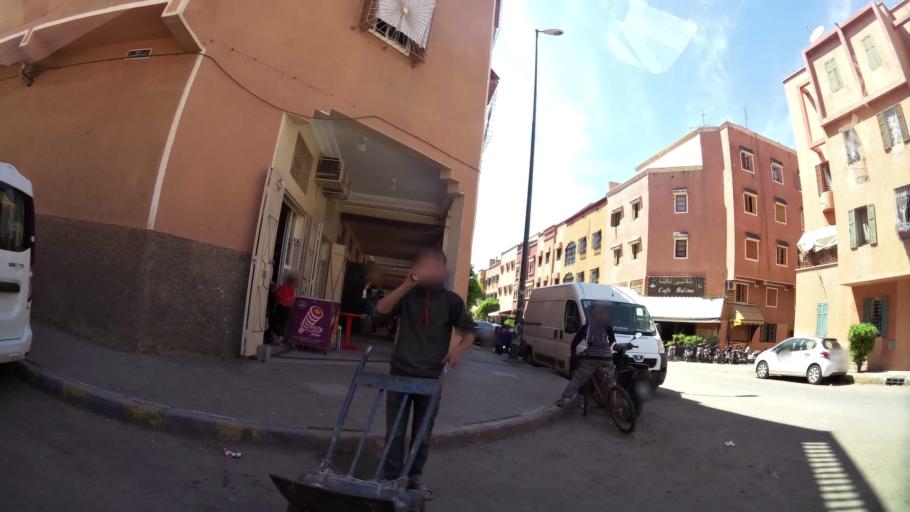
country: MA
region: Marrakech-Tensift-Al Haouz
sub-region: Marrakech
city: Marrakesh
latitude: 31.6465
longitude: -8.0657
